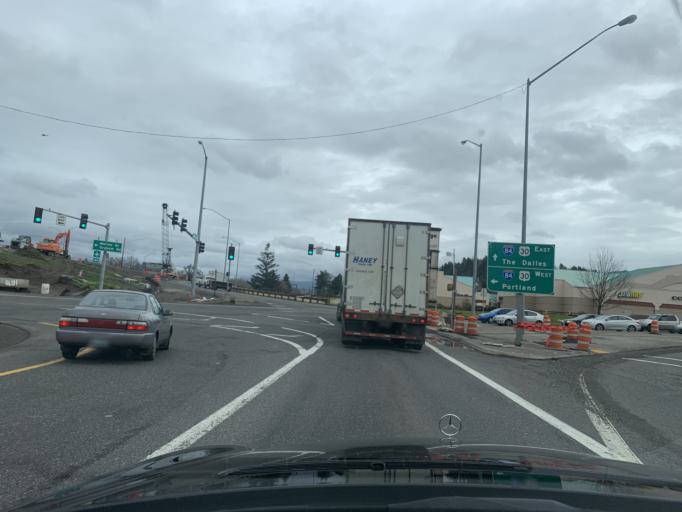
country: US
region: Oregon
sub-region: Multnomah County
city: Troutdale
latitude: 45.5444
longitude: -122.3911
